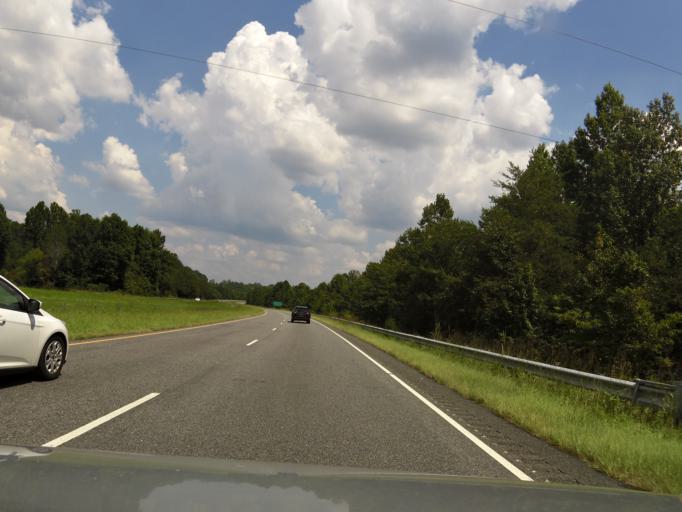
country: US
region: North Carolina
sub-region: Polk County
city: Columbus
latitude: 35.2732
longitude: -82.1359
